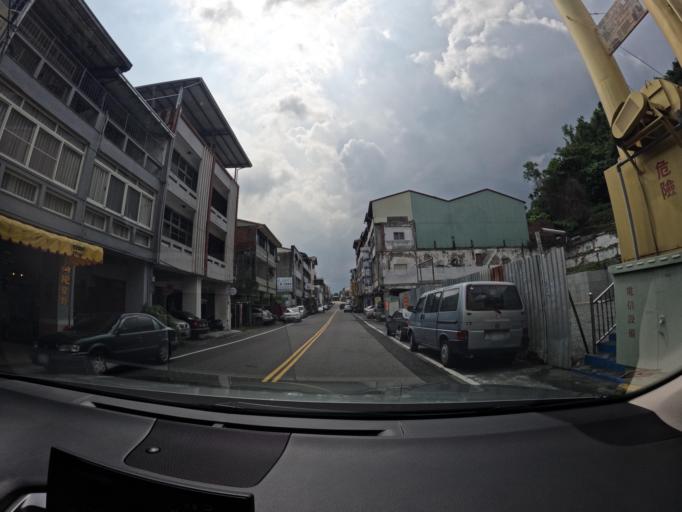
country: TW
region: Taiwan
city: Lugu
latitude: 23.8170
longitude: 120.8506
